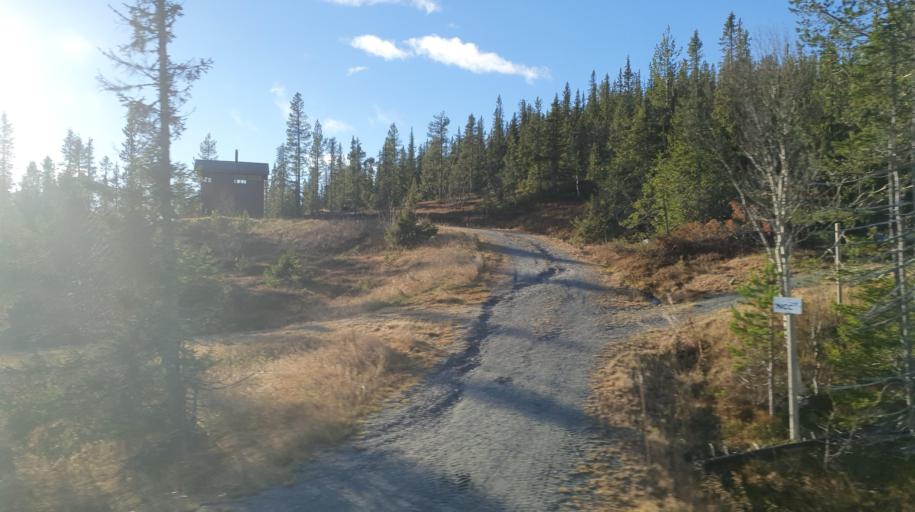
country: NO
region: Buskerud
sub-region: Krodsherad
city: Noresund
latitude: 60.2244
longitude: 9.5277
